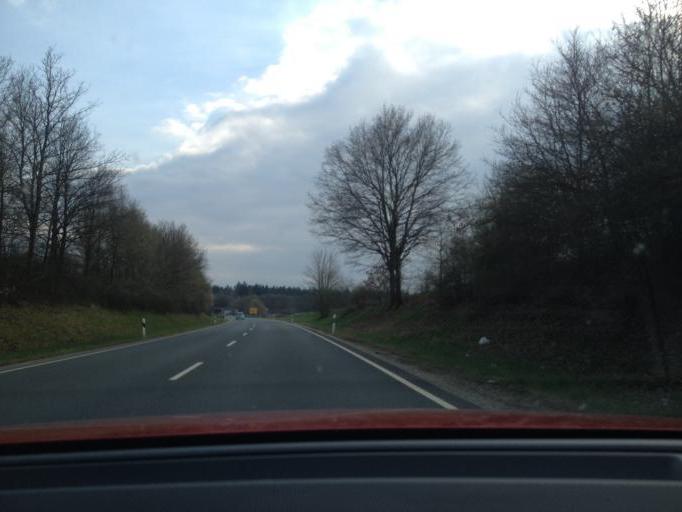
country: DE
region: Bavaria
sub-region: Upper Palatinate
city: Auerbach
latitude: 49.7043
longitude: 11.6115
